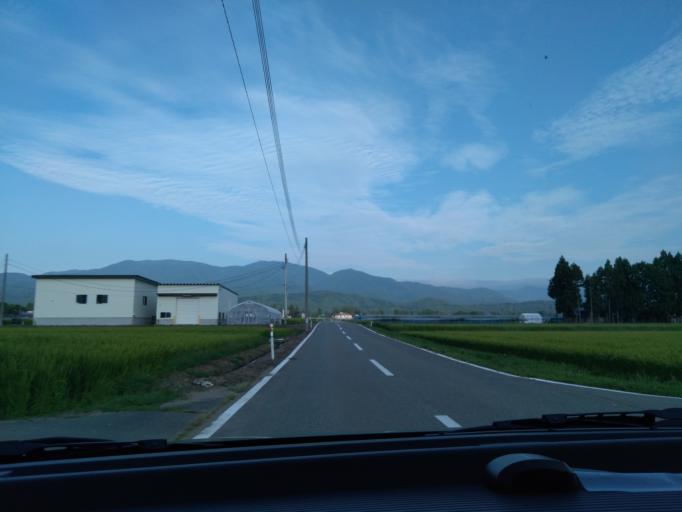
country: JP
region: Akita
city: Kakunodatemachi
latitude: 39.5736
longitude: 140.5893
